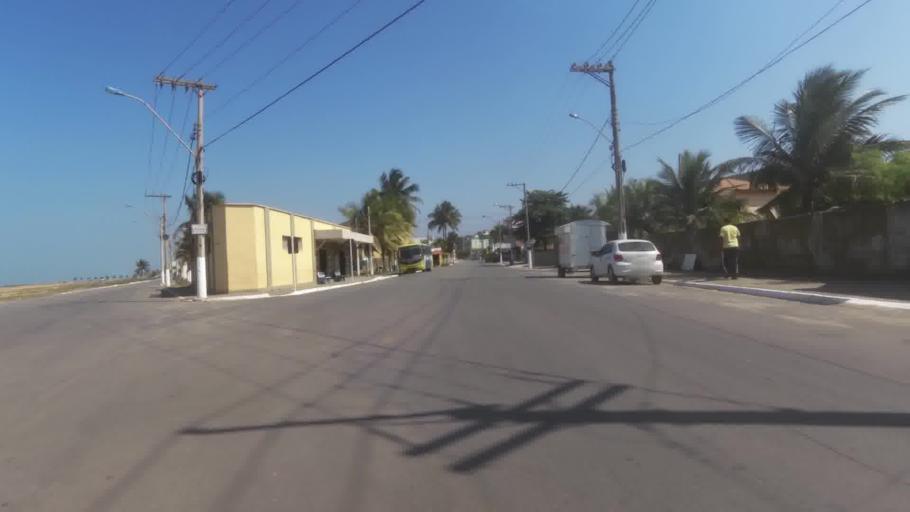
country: BR
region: Espirito Santo
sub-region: Marataizes
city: Marataizes
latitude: -21.0493
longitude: -40.8308
